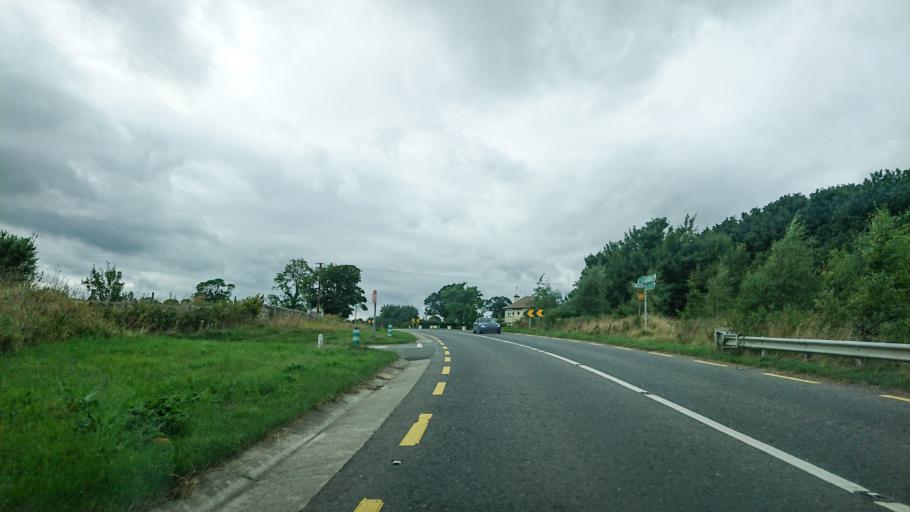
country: IE
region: Munster
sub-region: County Cork
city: Mallow
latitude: 52.1547
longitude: -8.5619
